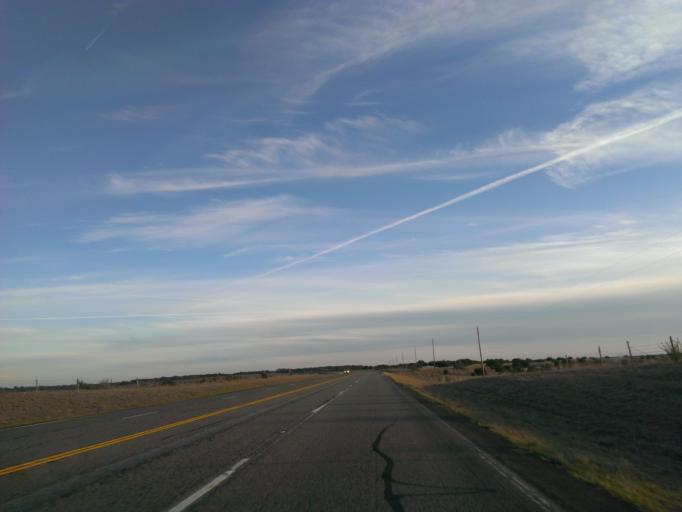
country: US
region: Texas
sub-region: Lampasas County
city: Kempner
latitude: 30.9067
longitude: -97.9719
